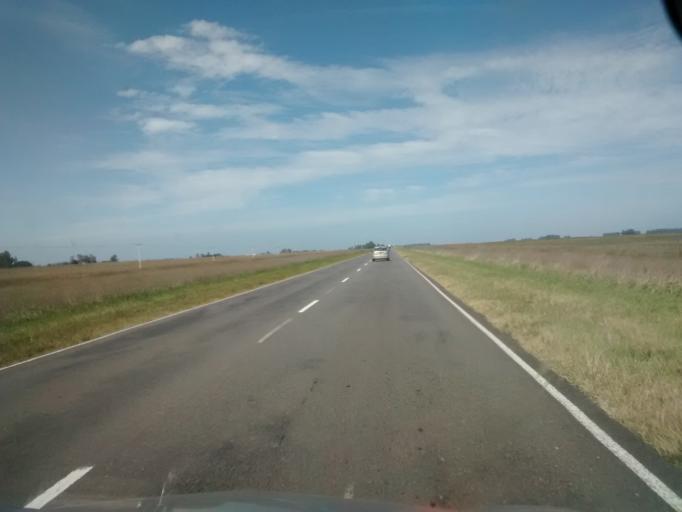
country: AR
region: Buenos Aires
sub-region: Partido de Ayacucho
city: Ayacucho
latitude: -36.6707
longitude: -58.5746
